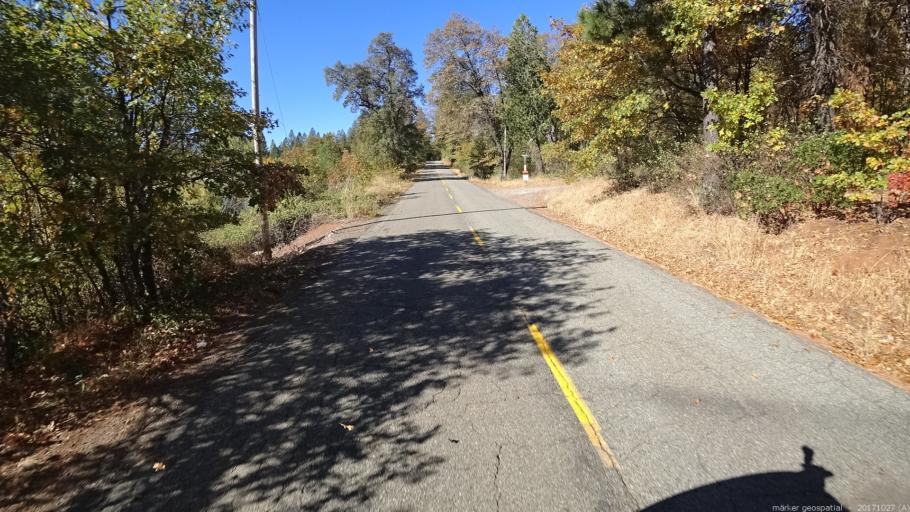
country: US
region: California
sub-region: Shasta County
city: Burney
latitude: 40.8262
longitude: -121.9450
